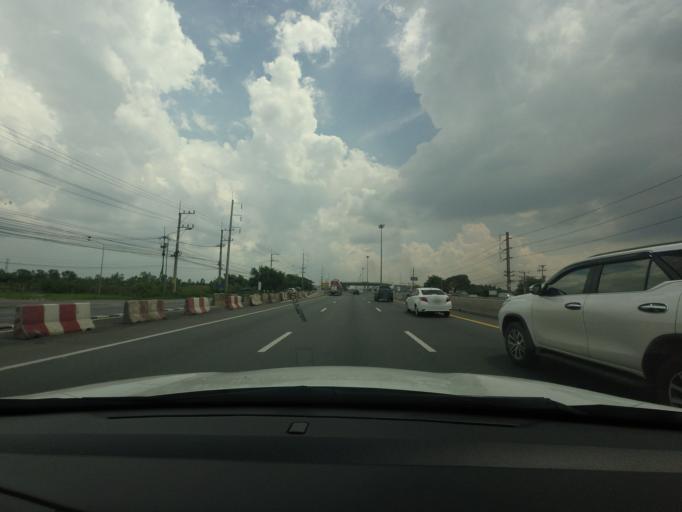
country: TH
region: Sara Buri
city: Nong Khae
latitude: 14.2968
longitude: 100.8240
